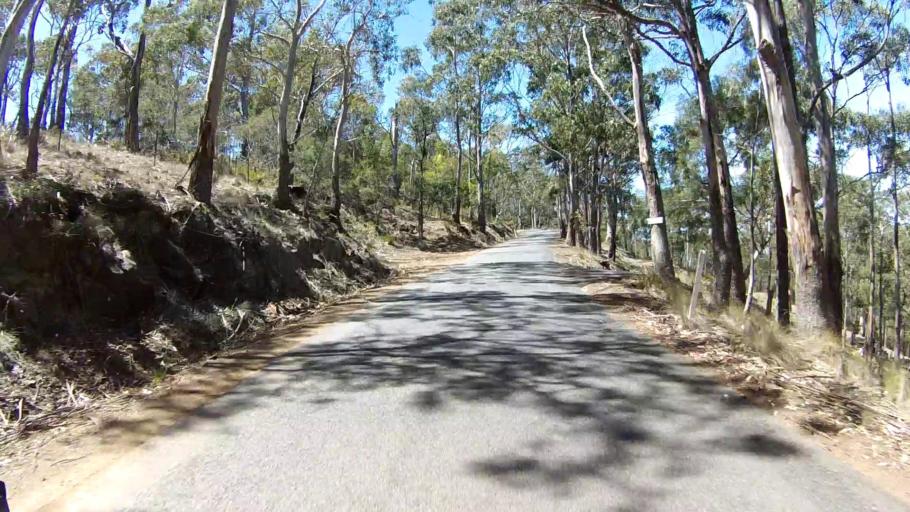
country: AU
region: Tasmania
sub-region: Clarence
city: Cambridge
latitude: -42.8556
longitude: 147.4387
